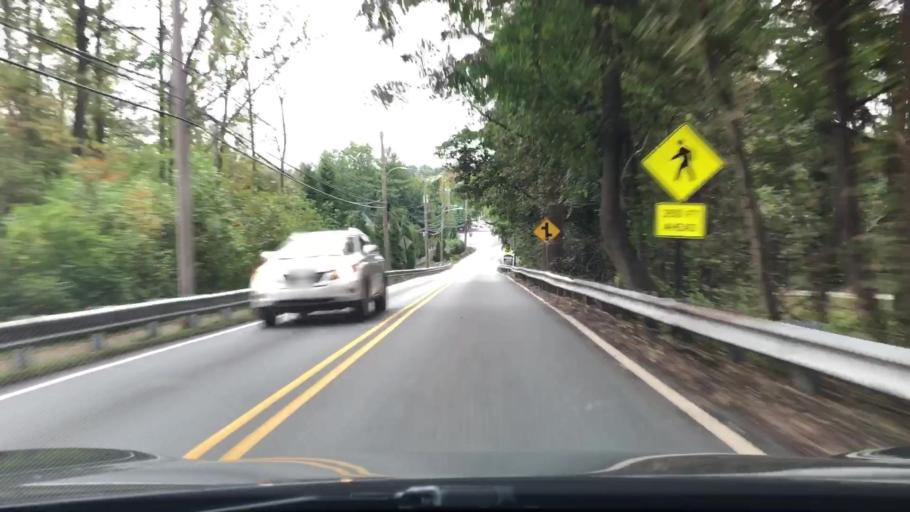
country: US
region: Pennsylvania
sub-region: Delaware County
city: Radnor
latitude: 40.0372
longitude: -75.3663
